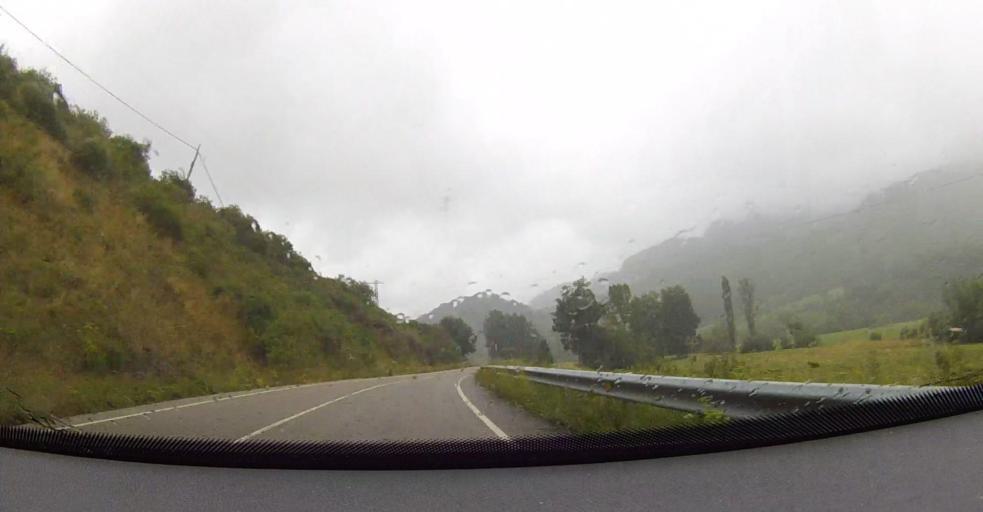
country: ES
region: Castille and Leon
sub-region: Provincia de Leon
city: Acebedo
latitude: 43.0403
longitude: -5.1066
